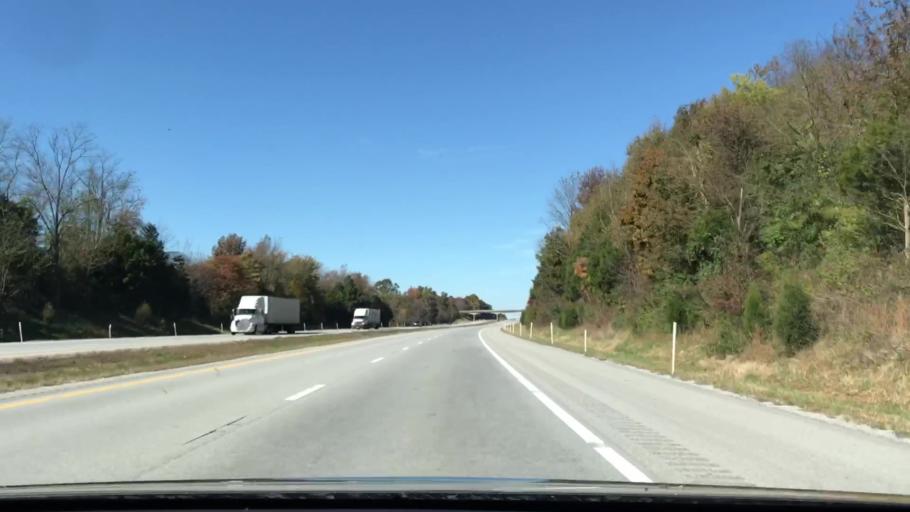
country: US
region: Kentucky
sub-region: Barren County
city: Glasgow
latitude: 37.0152
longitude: -86.0285
